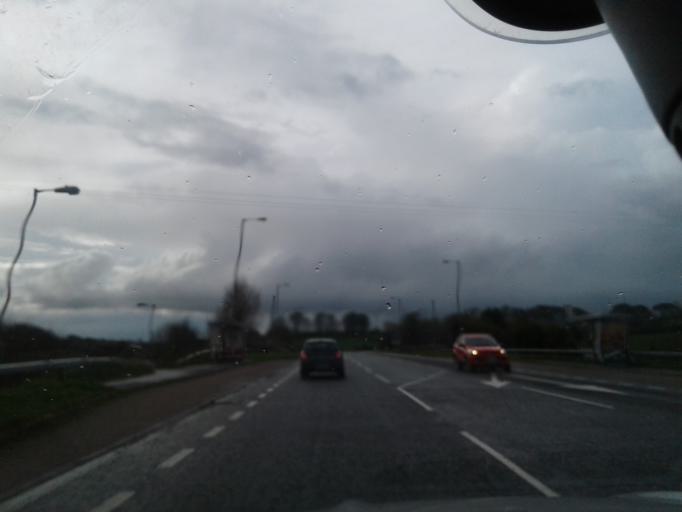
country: GB
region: Northern Ireland
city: Newtownstewart
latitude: 54.7216
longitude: -7.3724
